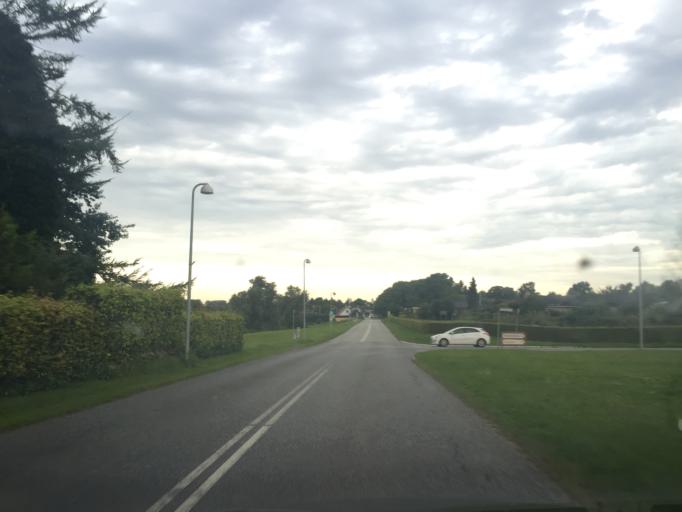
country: DK
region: Zealand
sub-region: Roskilde Kommune
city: Gundsomagle
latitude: 55.7338
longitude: 12.1612
